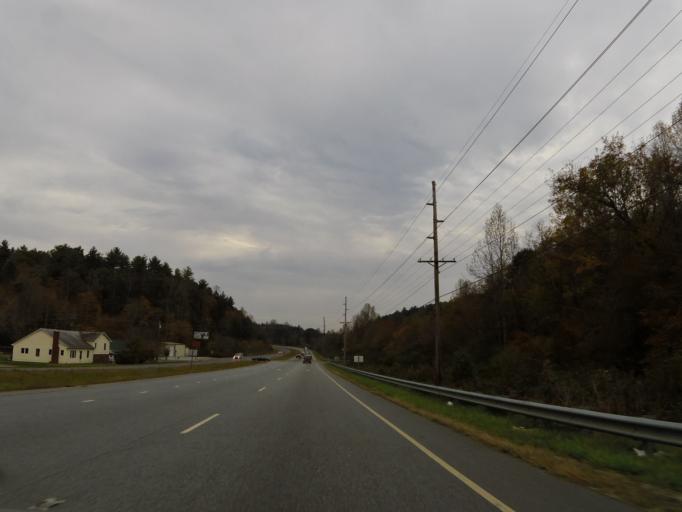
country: US
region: North Carolina
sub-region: Caldwell County
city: Lenoir
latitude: 35.9454
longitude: -81.5468
